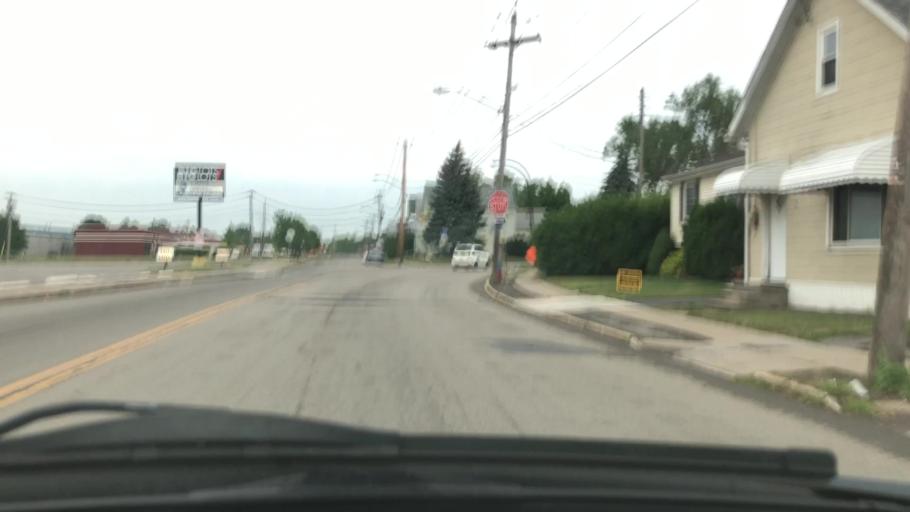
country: US
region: New York
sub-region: Erie County
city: Sloan
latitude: 42.8808
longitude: -78.8011
